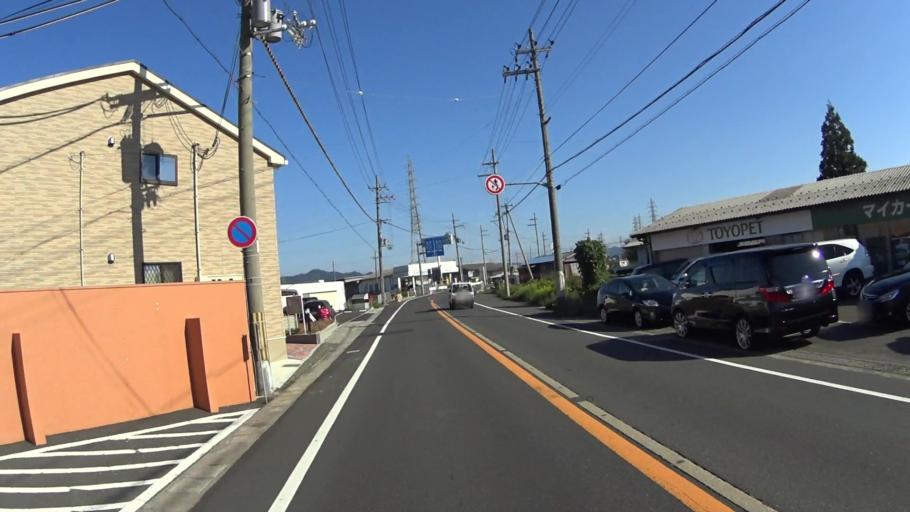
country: JP
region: Kyoto
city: Miyazu
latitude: 35.6115
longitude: 135.0670
